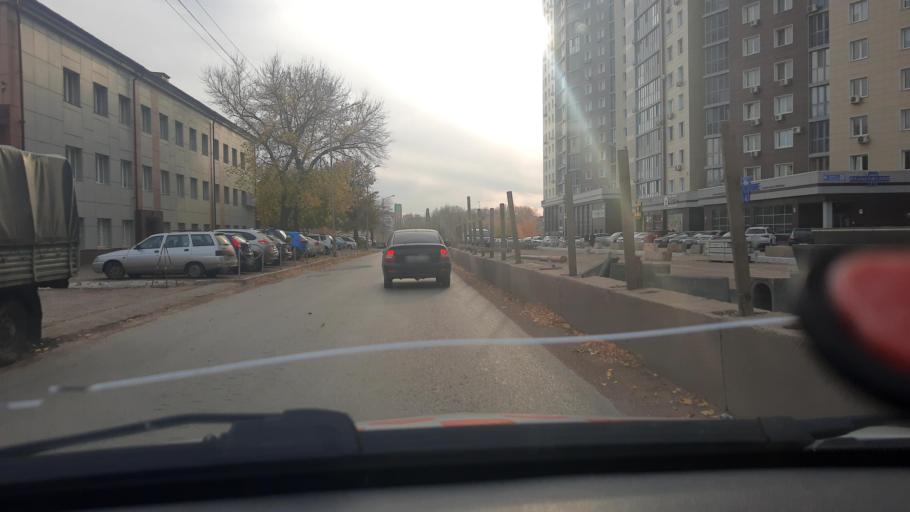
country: RU
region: Bashkortostan
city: Ufa
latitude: 54.7561
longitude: 56.0107
